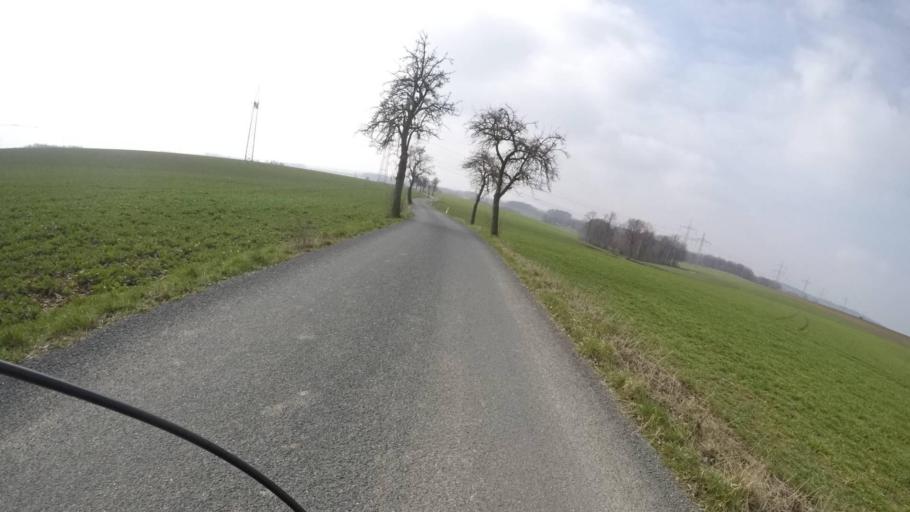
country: DE
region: Saxony
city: Niederfrohna
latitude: 50.8798
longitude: 12.6974
